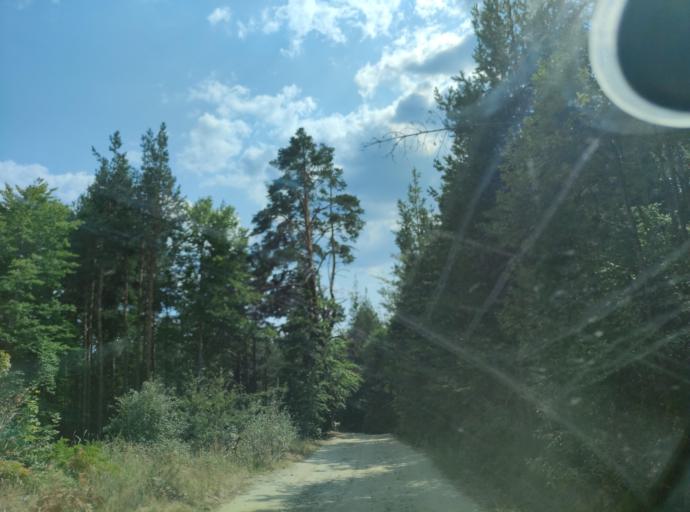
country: BG
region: Blagoevgrad
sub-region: Obshtina Belitsa
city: Belitsa
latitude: 42.0285
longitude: 23.5823
